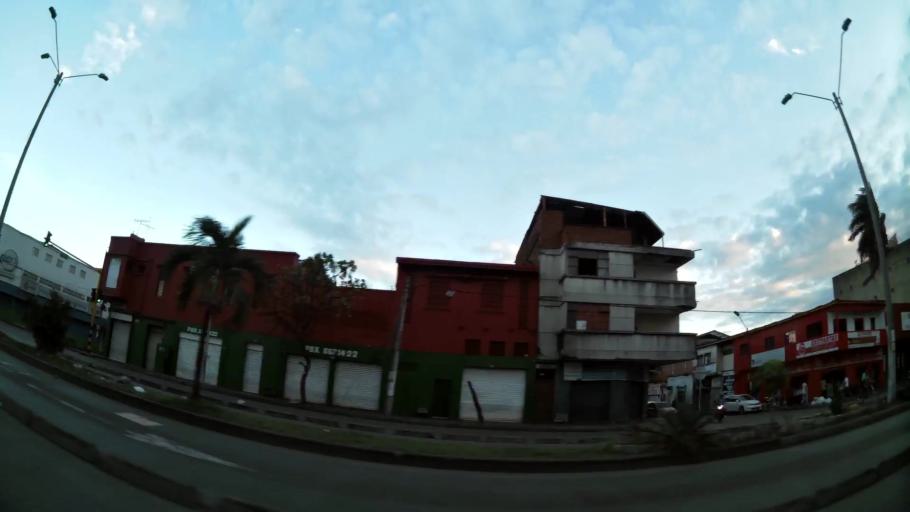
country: CO
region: Valle del Cauca
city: Cali
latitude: 3.4439
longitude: -76.5216
